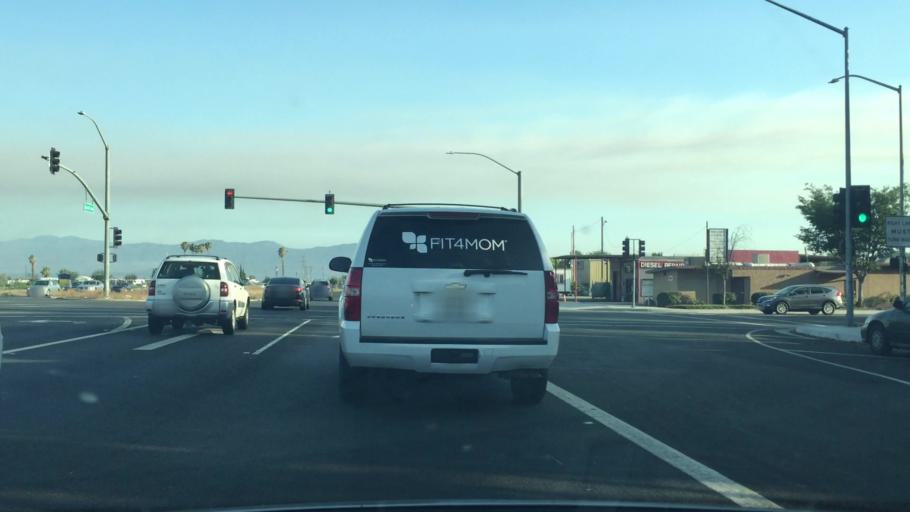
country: US
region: California
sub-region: San Bernardino County
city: Chino
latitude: 34.0124
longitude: -117.6509
